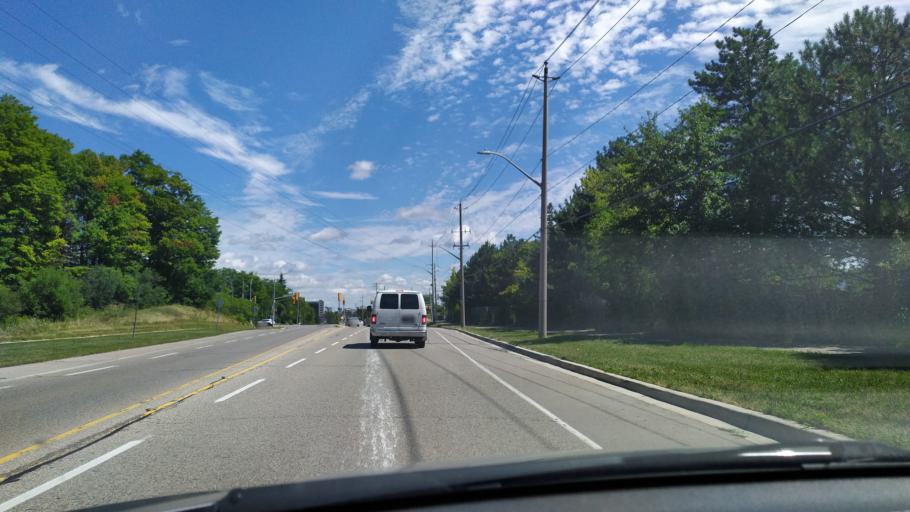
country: CA
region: Ontario
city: Kitchener
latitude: 43.4358
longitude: -80.5308
